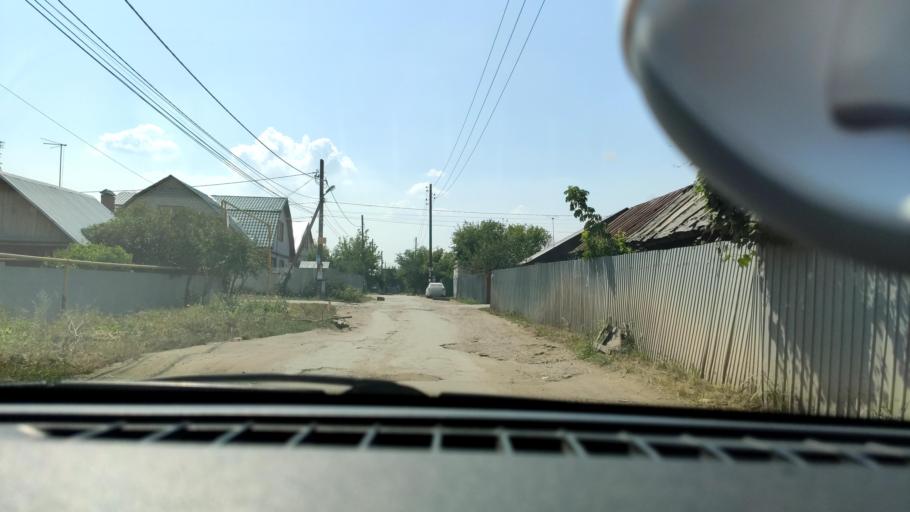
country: RU
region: Samara
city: Samara
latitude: 53.1412
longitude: 50.0966
